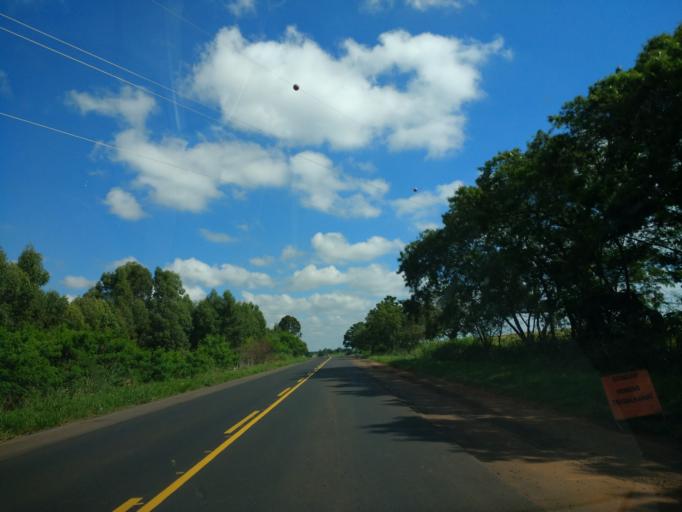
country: BR
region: Parana
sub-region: Umuarama
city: Umuarama
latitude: -23.8663
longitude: -53.3911
